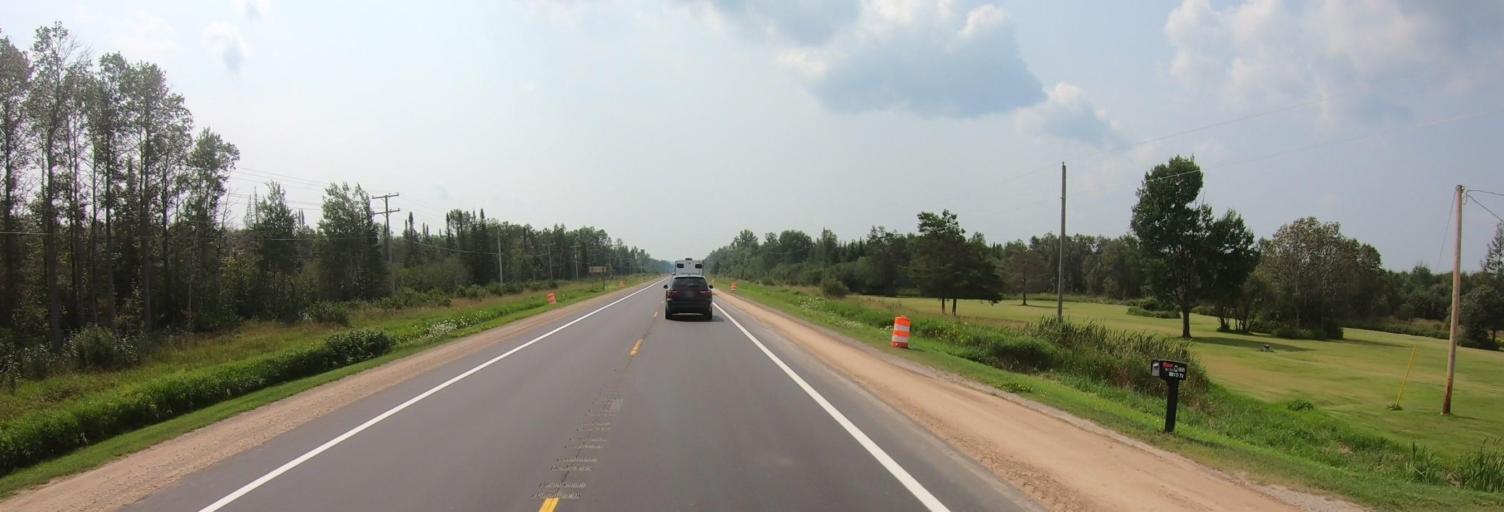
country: US
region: Michigan
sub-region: Luce County
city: Newberry
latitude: 46.3967
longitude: -85.5099
